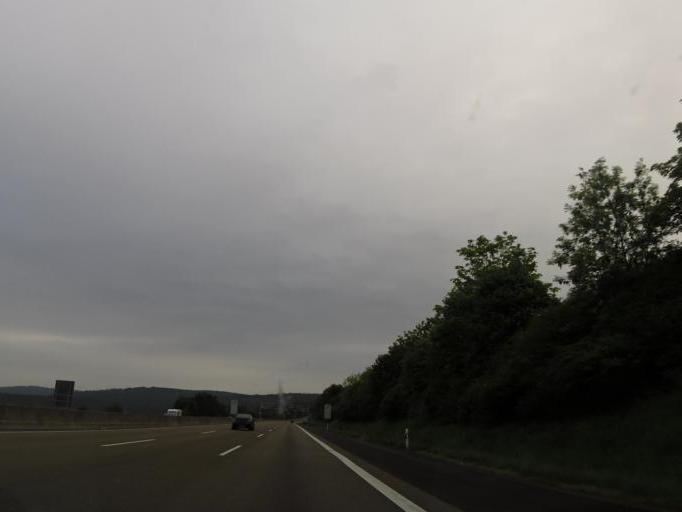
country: DE
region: Hesse
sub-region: Regierungsbezirk Kassel
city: Guxhagen
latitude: 51.1888
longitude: 9.4720
